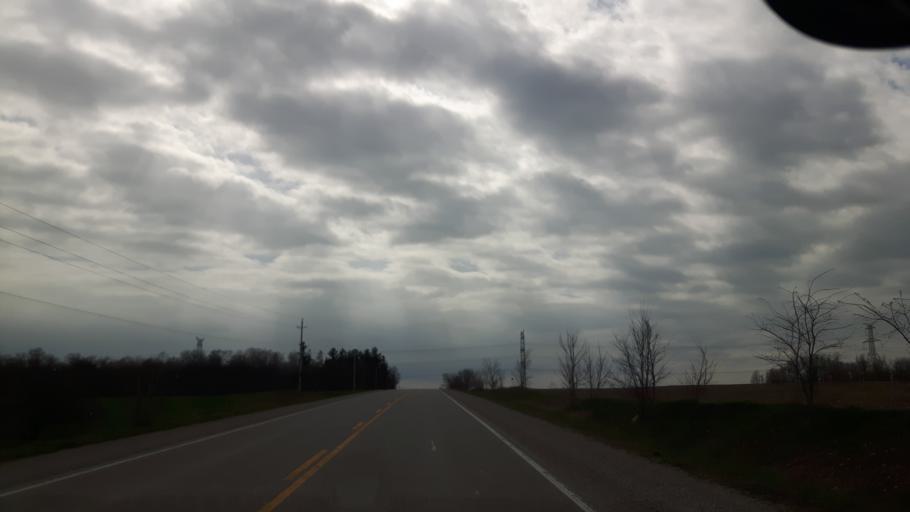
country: CA
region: Ontario
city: Bluewater
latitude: 43.5869
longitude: -81.6264
